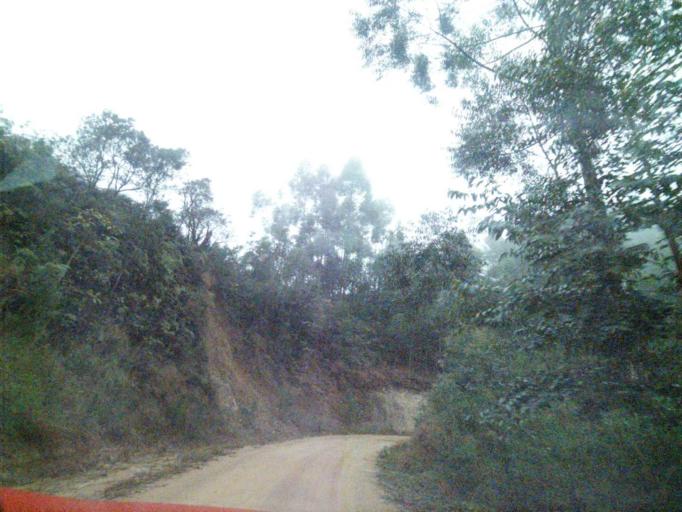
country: BR
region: Santa Catarina
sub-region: Anitapolis
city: Anitapolis
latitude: -27.9154
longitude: -49.0963
